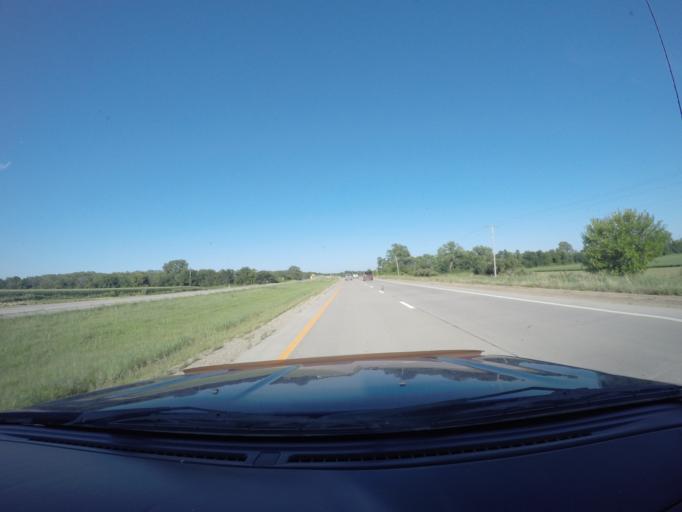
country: US
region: Kansas
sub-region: Shawnee County
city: Topeka
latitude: 39.0870
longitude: -95.5310
